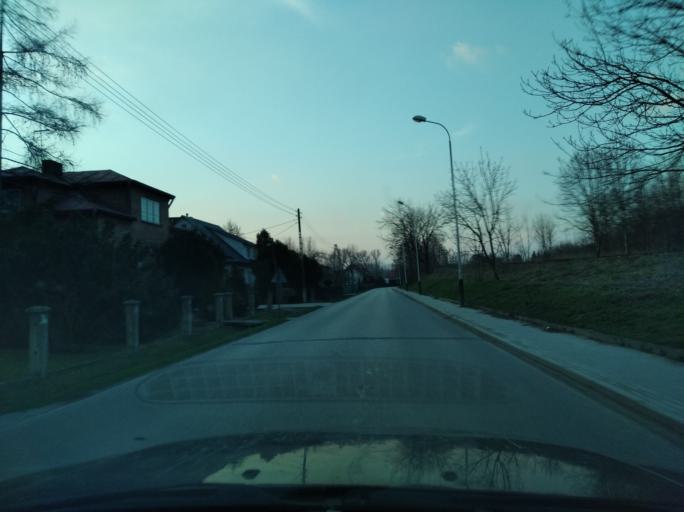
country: PL
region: Subcarpathian Voivodeship
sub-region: Powiat przeworski
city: Przeworsk
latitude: 50.0446
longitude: 22.5037
